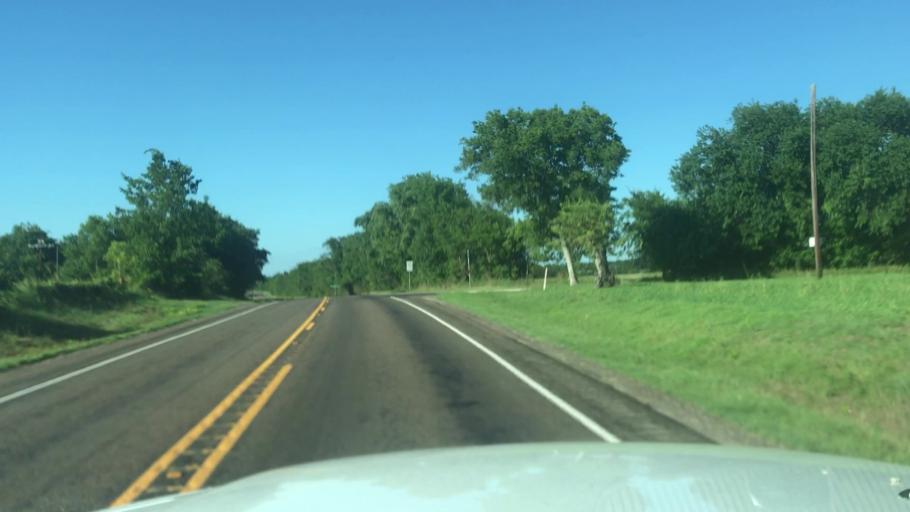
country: US
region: Texas
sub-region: Grimes County
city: Anderson
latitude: 30.6383
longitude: -95.8599
